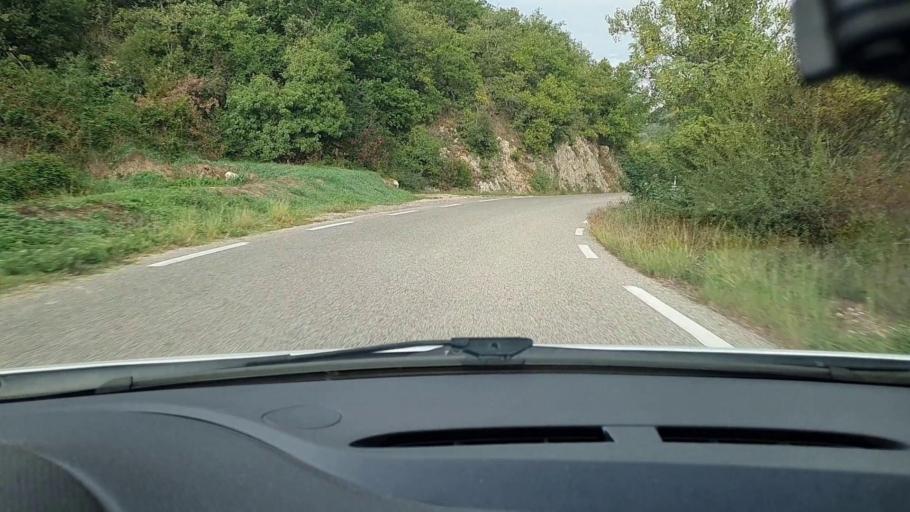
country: FR
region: Languedoc-Roussillon
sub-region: Departement du Gard
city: Barjac
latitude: 44.2418
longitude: 4.3040
